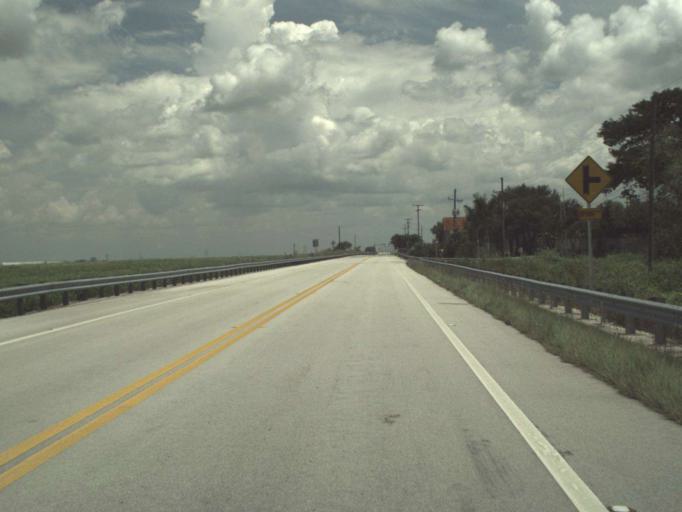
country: US
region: Florida
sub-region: Palm Beach County
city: Pahokee
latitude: 26.8507
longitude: -80.6137
